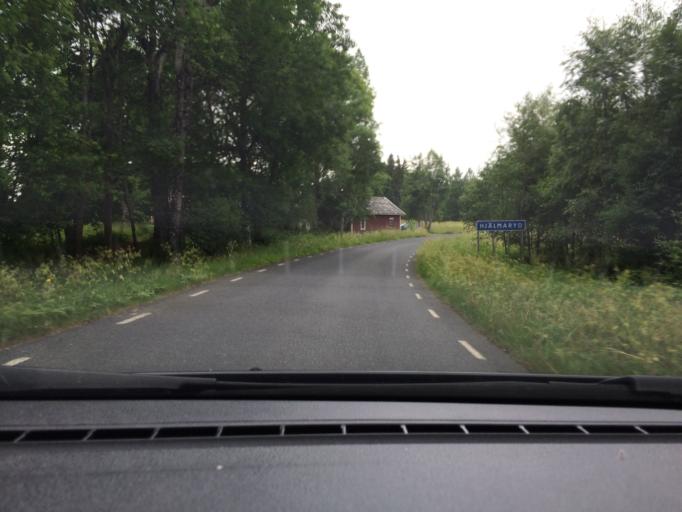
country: SE
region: Joenkoeping
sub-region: Varnamo Kommun
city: Forsheda
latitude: 57.0796
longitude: 13.8134
